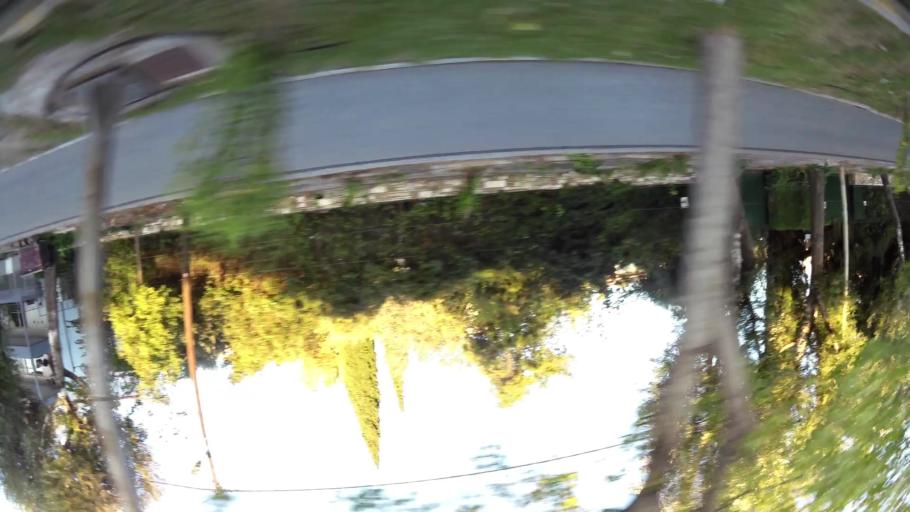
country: GR
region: Attica
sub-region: Nomarchia Athinas
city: Kifisia
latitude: 38.0817
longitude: 23.8194
